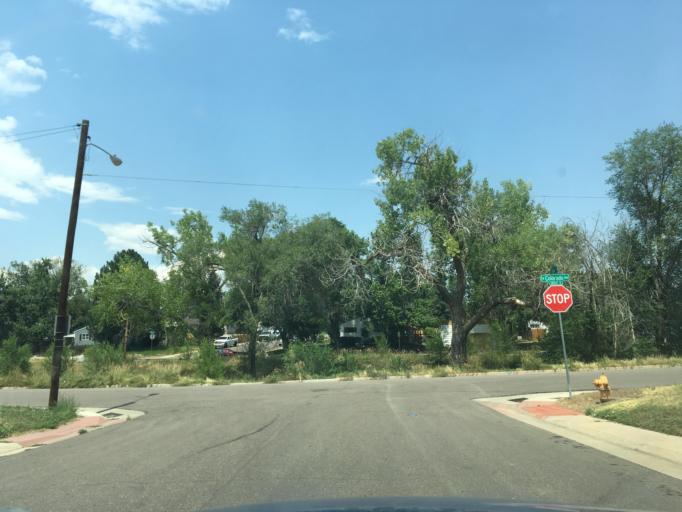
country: US
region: Colorado
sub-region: Arapahoe County
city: Sheridan
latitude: 39.6846
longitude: -105.0319
